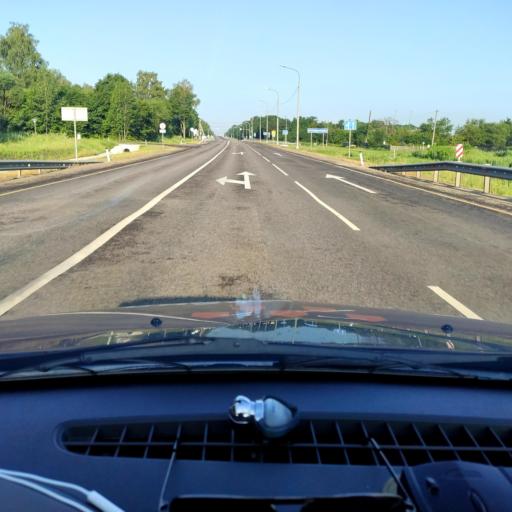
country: RU
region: Lipetsk
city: Izmalkovo
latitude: 52.4414
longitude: 37.9544
